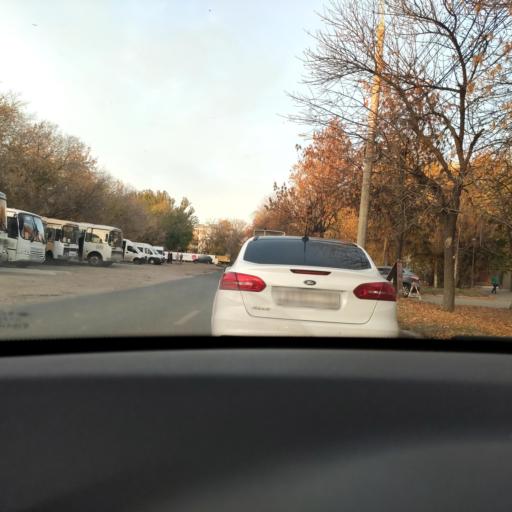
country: RU
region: Samara
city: Samara
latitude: 53.1855
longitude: 50.1729
